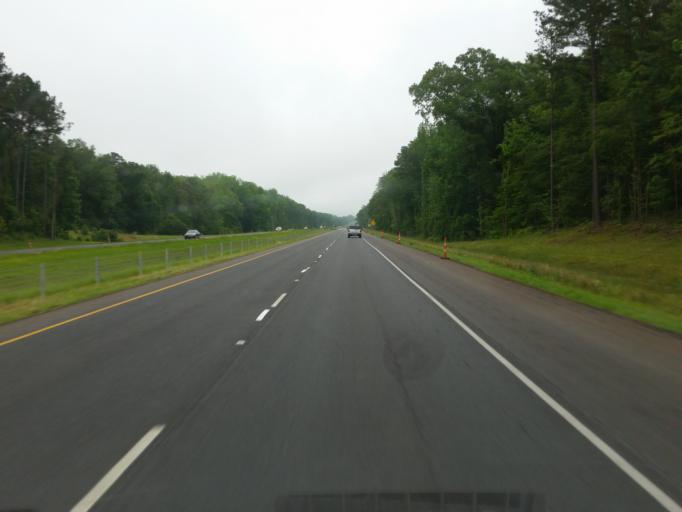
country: US
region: Louisiana
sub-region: Bienville Parish
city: Arcadia
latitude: 32.5629
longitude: -93.1023
